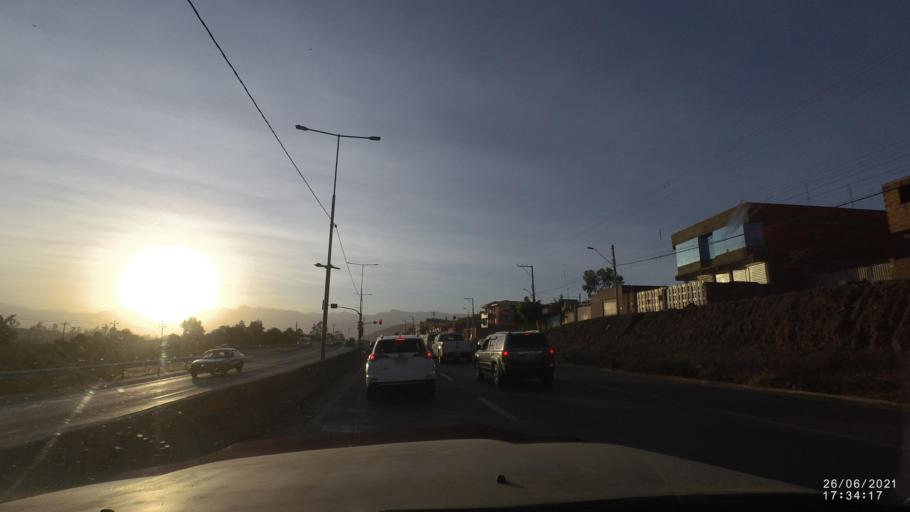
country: BO
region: Cochabamba
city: Cochabamba
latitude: -17.4628
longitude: -66.1217
